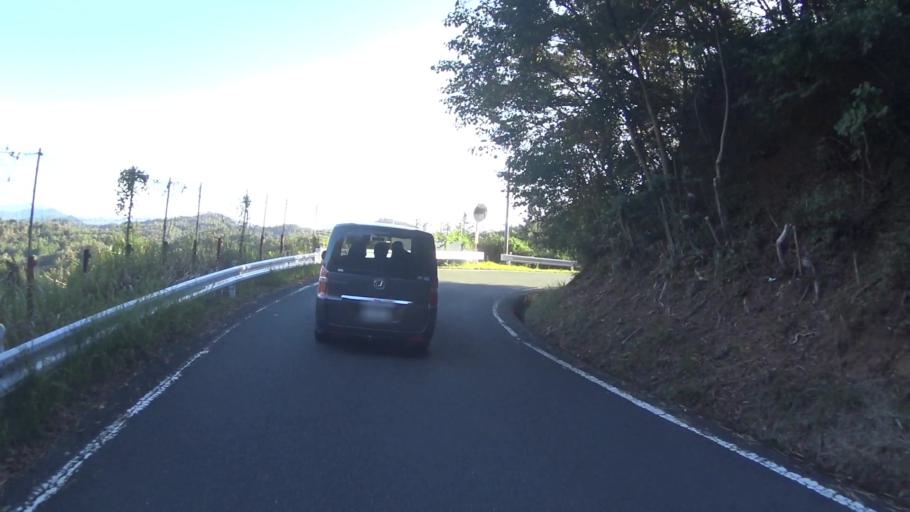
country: JP
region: Hyogo
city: Toyooka
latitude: 35.6133
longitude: 134.8765
